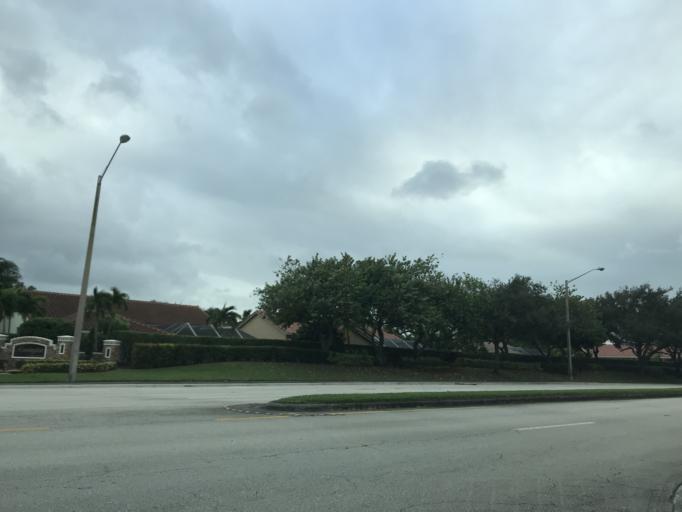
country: US
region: Florida
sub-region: Broward County
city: Coral Springs
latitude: 26.2982
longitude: -80.2748
